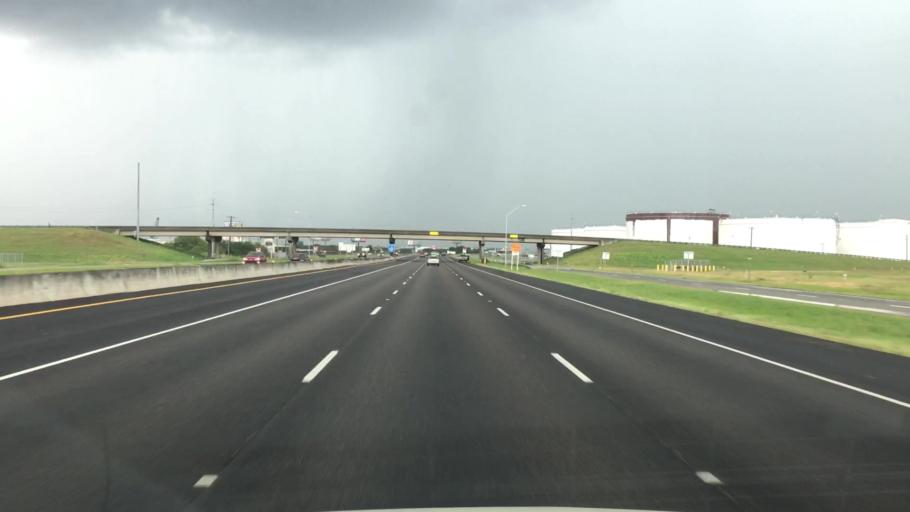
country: US
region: Texas
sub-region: Nueces County
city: Corpus Christi
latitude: 27.8105
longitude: -97.5008
